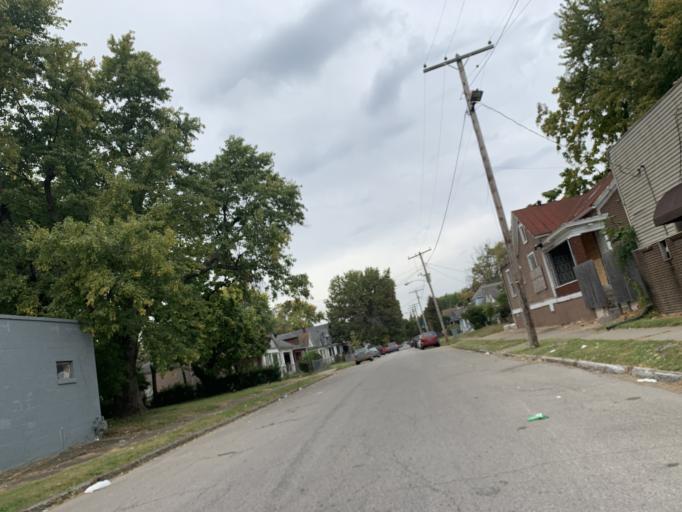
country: US
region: Kentucky
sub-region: Jefferson County
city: Louisville
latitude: 38.2419
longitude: -85.7851
